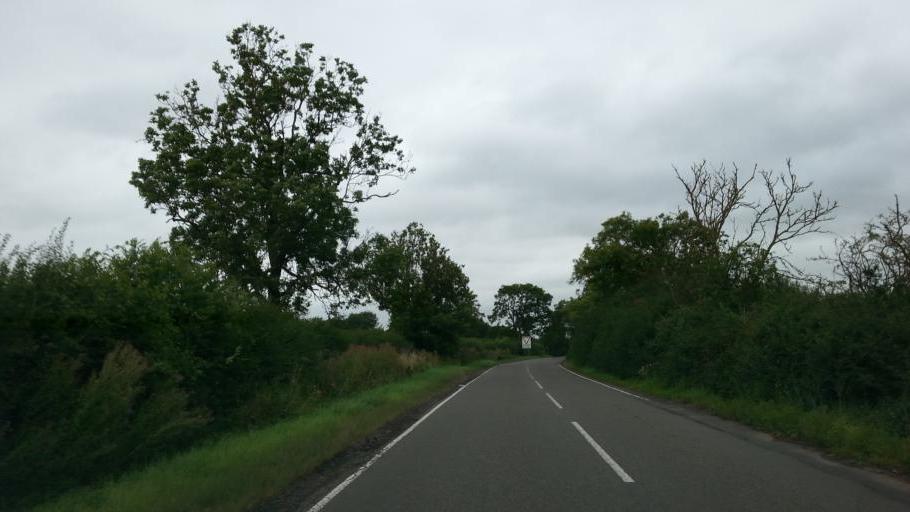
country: GB
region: England
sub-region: Nottinghamshire
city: Southwell
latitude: 53.1253
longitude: -0.8876
